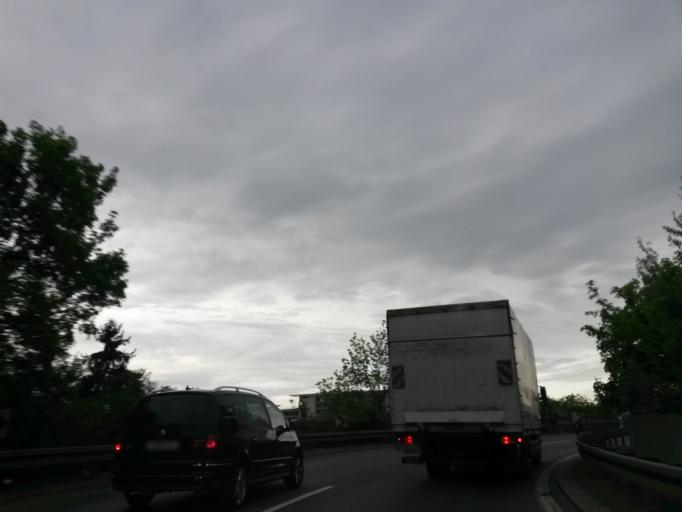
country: DE
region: Baden-Wuerttemberg
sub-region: Regierungsbezirk Stuttgart
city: Stuttgart Feuerbach
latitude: 48.8229
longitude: 9.1767
